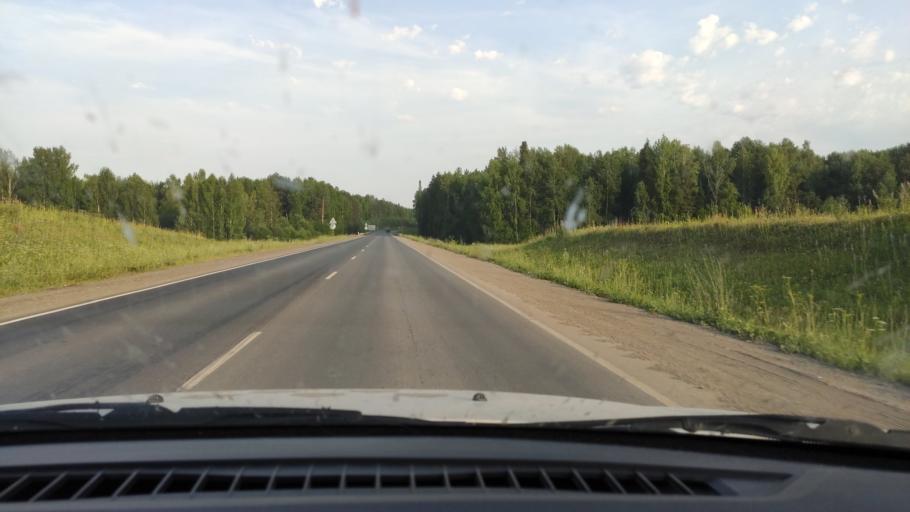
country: RU
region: Perm
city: Siva
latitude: 58.4502
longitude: 54.4212
